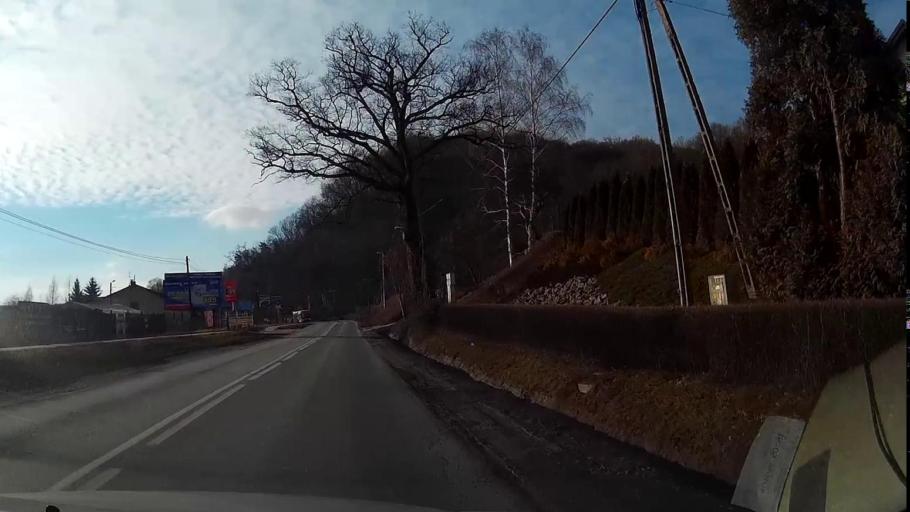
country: PL
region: Lesser Poland Voivodeship
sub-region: Powiat krakowski
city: Kryspinow
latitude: 50.0439
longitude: 19.8490
